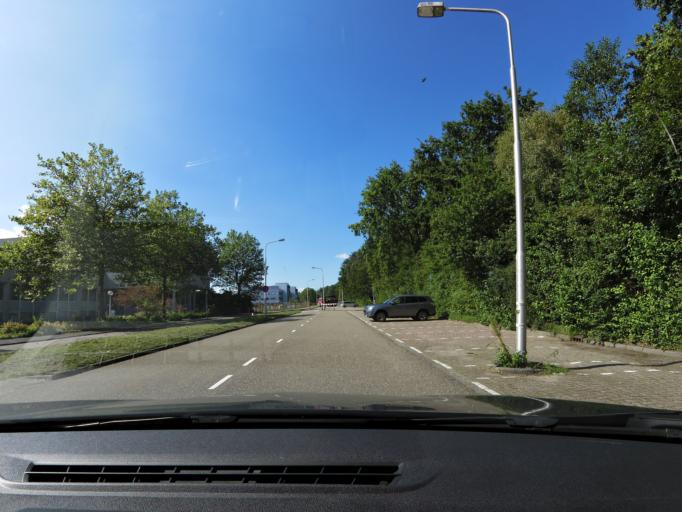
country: NL
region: North Holland
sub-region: Gemeente Amstelveen
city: Amstelveen
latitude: 52.2870
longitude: 4.8514
